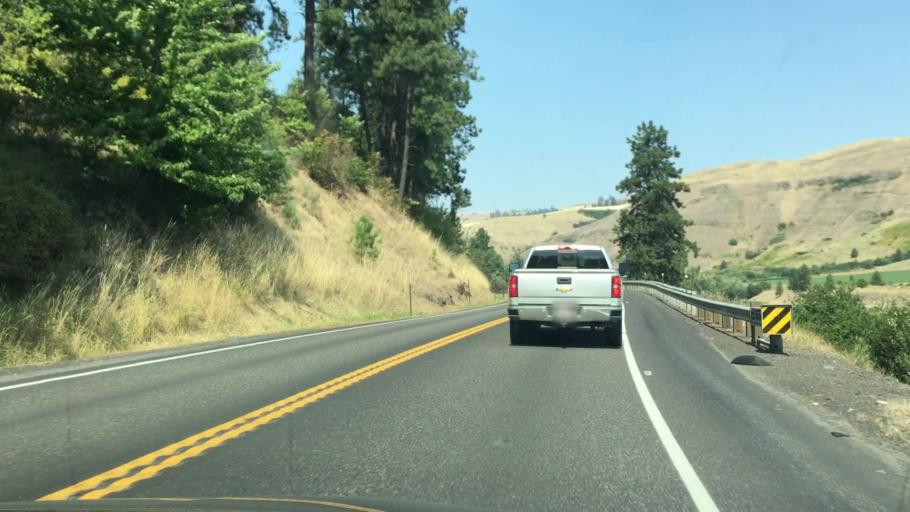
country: US
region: Idaho
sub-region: Clearwater County
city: Orofino
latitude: 46.5009
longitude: -116.5015
